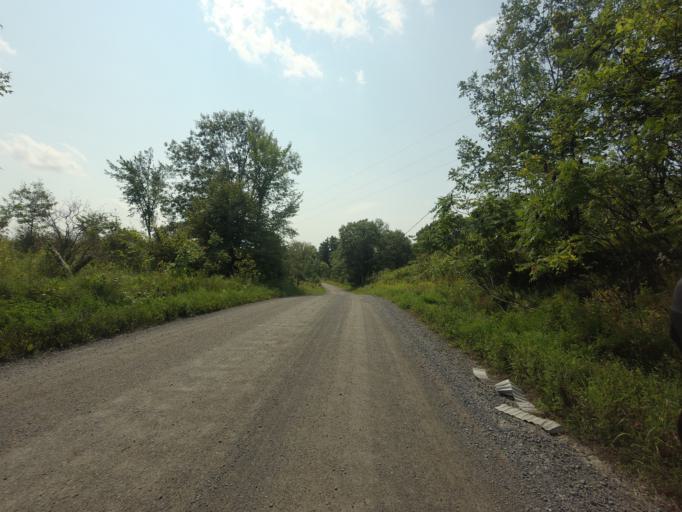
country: CA
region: Ontario
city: Kingston
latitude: 44.6432
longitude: -76.6567
